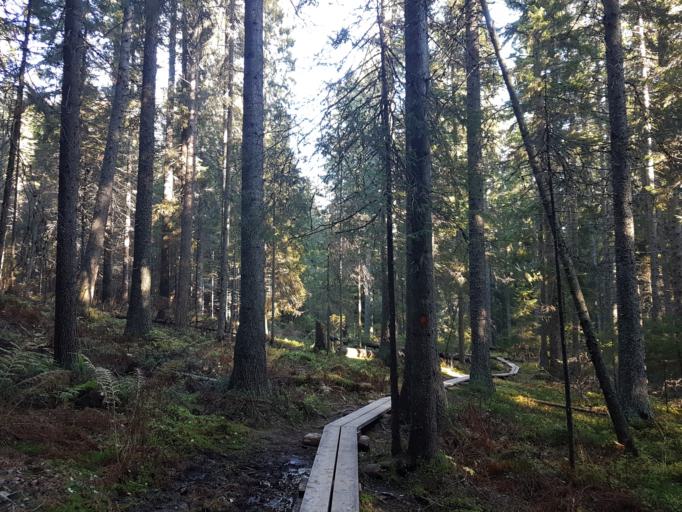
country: SE
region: Vaesternorrland
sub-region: OErnskoeldsviks Kommun
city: Kopmanholmen
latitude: 63.0908
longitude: 18.4964
